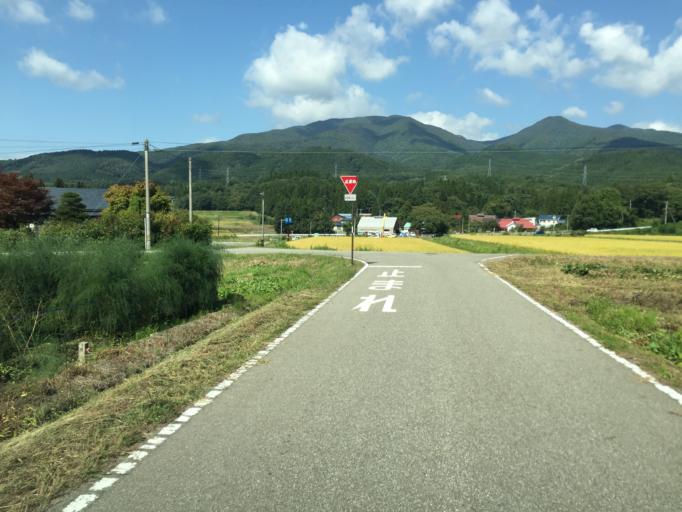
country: JP
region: Fukushima
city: Inawashiro
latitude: 37.5606
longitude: 140.0049
